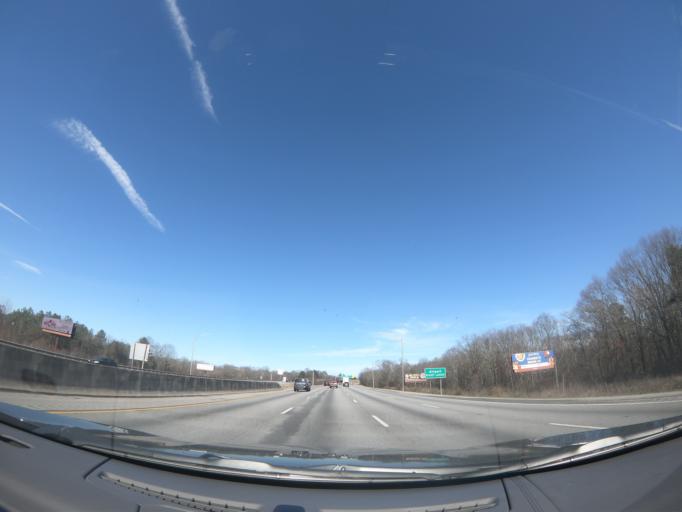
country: US
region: Tennessee
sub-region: Hamilton County
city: East Ridge
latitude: 34.9984
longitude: -85.2094
